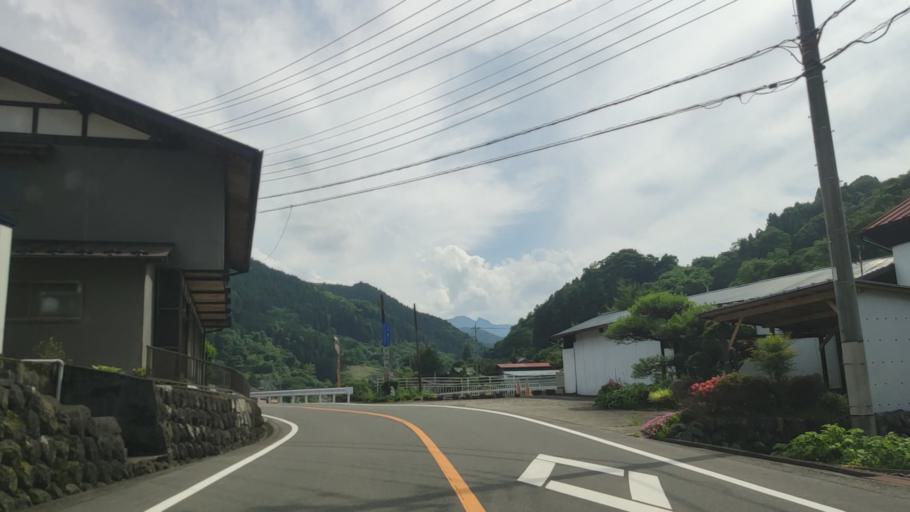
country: JP
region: Gunma
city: Tomioka
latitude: 36.1831
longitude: 138.7455
